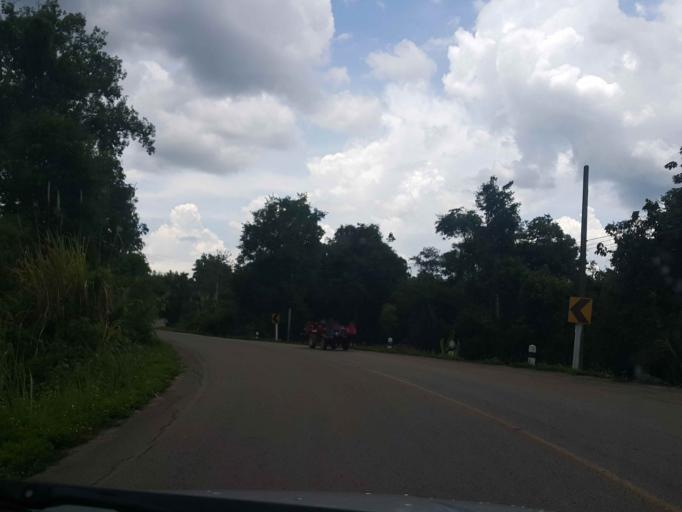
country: TH
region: Lampang
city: Ngao
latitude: 18.9374
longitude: 100.0798
